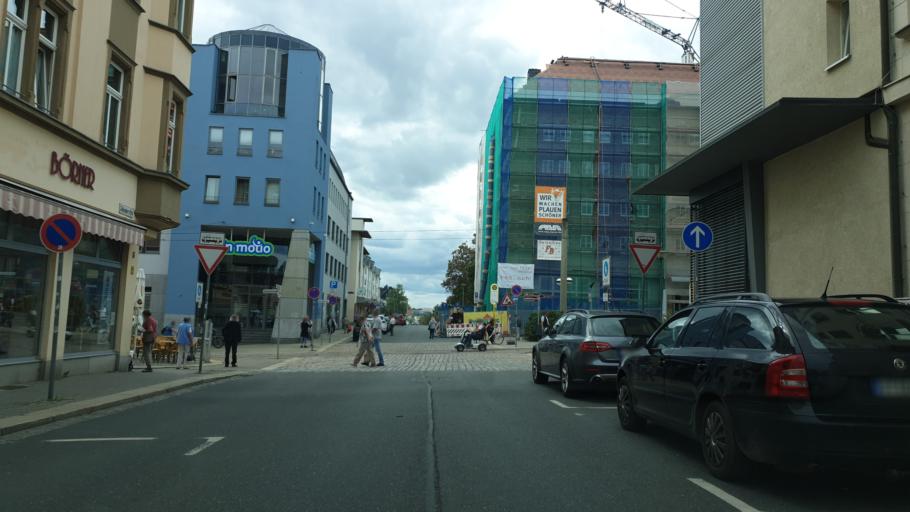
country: DE
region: Saxony
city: Plauen
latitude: 50.5017
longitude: 12.1361
